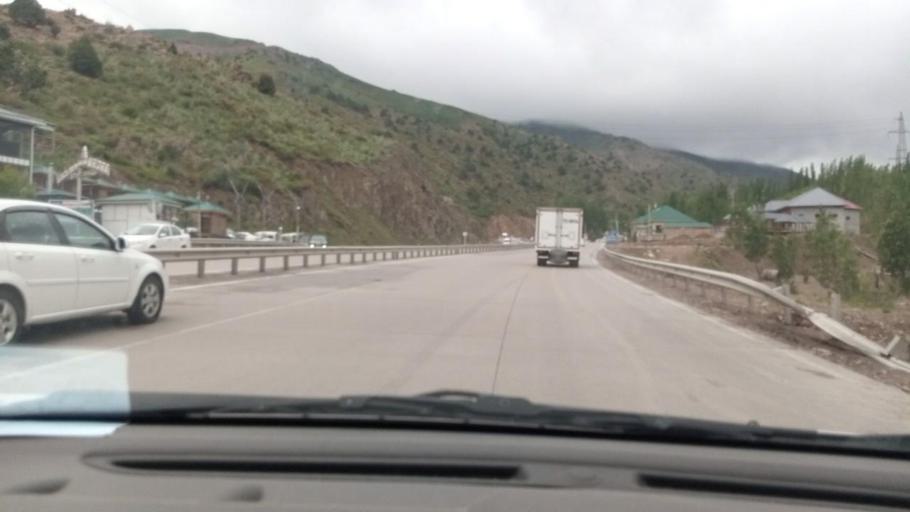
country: TJ
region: Viloyati Sughd
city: Shaydon
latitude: 41.0330
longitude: 70.5893
